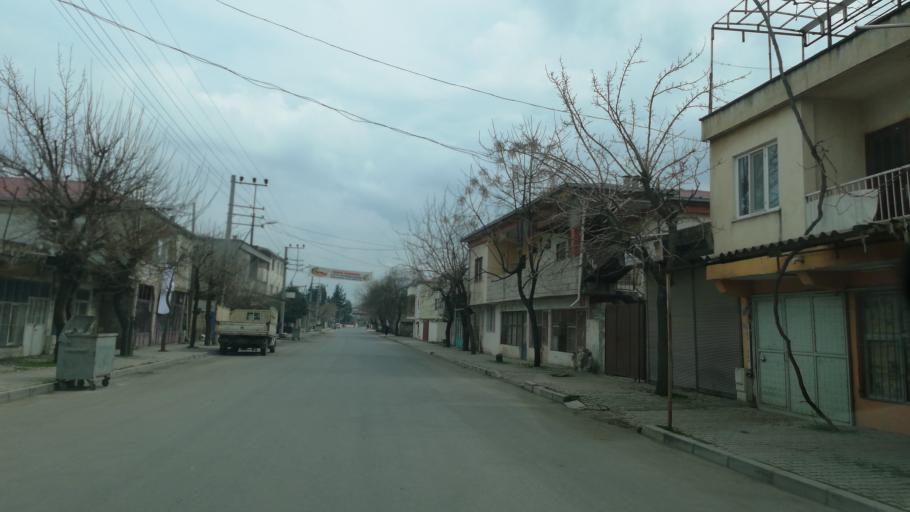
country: TR
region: Kahramanmaras
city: Turkoglu
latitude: 37.4118
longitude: 36.8807
